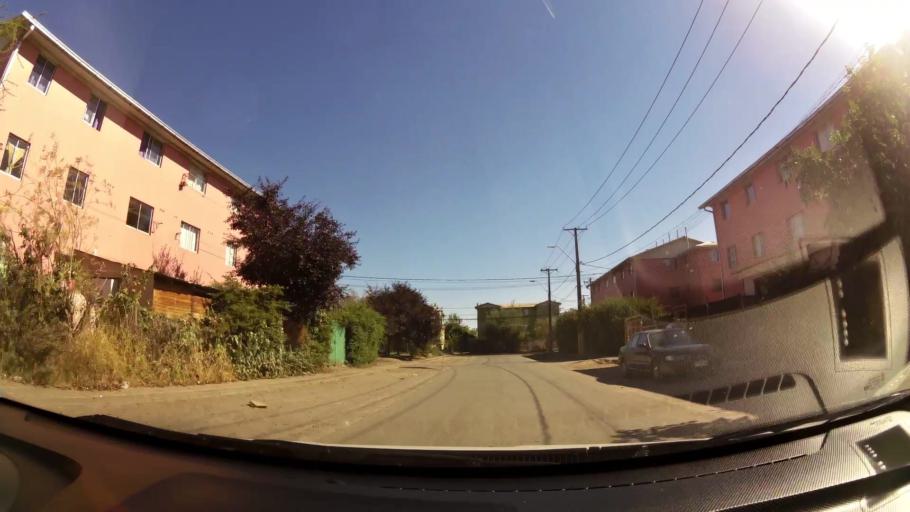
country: CL
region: O'Higgins
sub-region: Provincia de Colchagua
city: Chimbarongo
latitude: -34.5736
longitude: -71.0001
